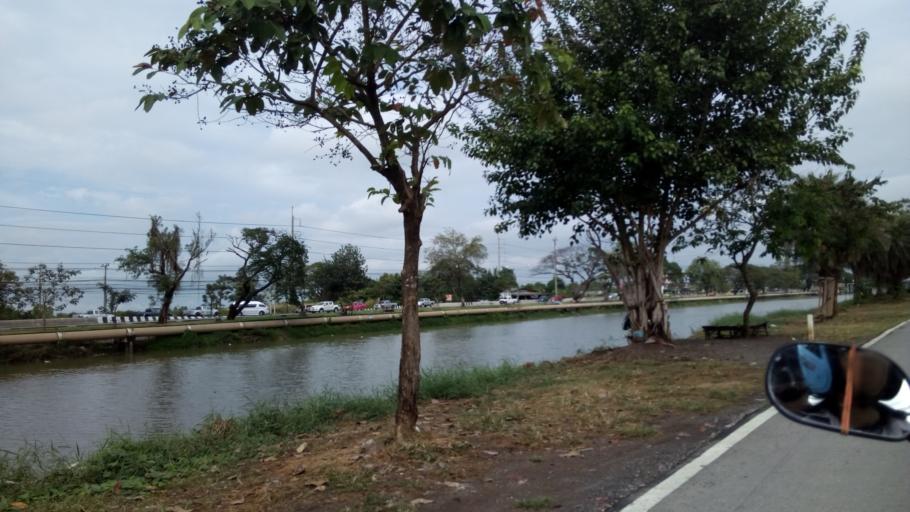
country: TH
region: Pathum Thani
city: Nong Suea
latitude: 14.0643
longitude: 100.8596
